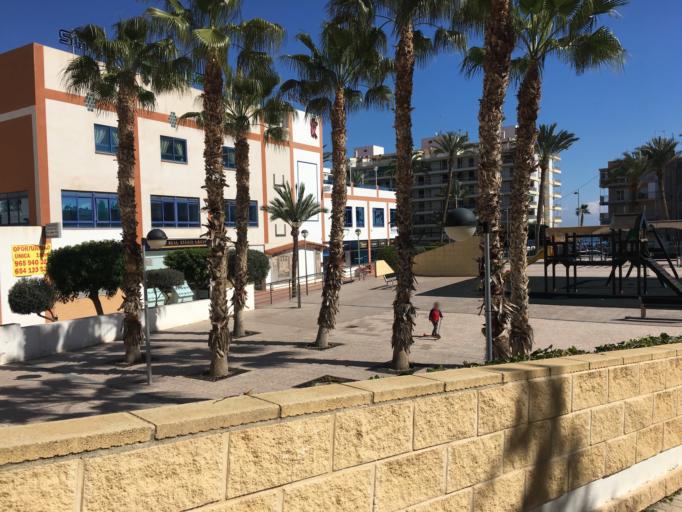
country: ES
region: Valencia
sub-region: Provincia de Alicante
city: el Campello
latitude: 38.4235
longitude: -0.3924
